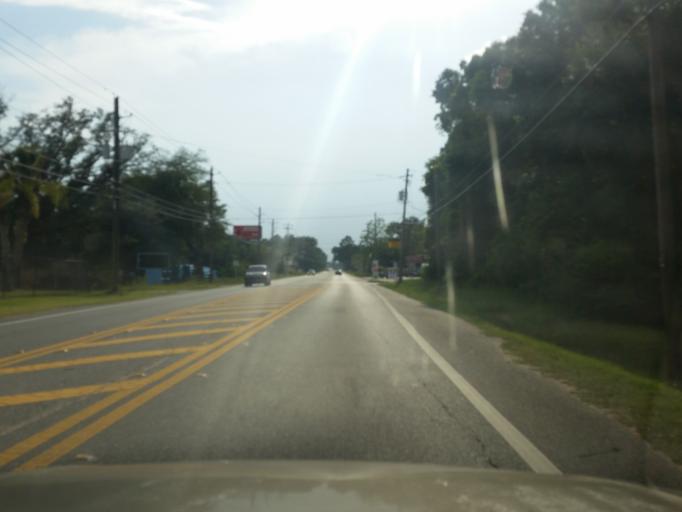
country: US
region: Florida
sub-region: Escambia County
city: Ferry Pass
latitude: 30.5101
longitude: -87.2078
